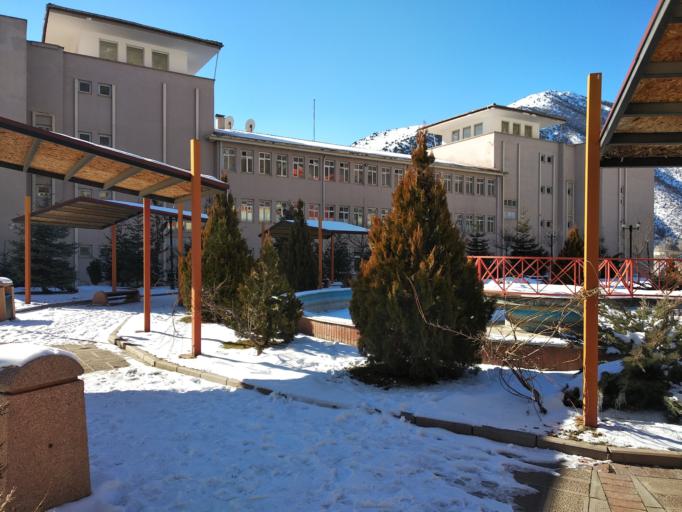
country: TR
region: Gumushane
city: Gumushkhane
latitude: 40.4361
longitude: 39.5162
